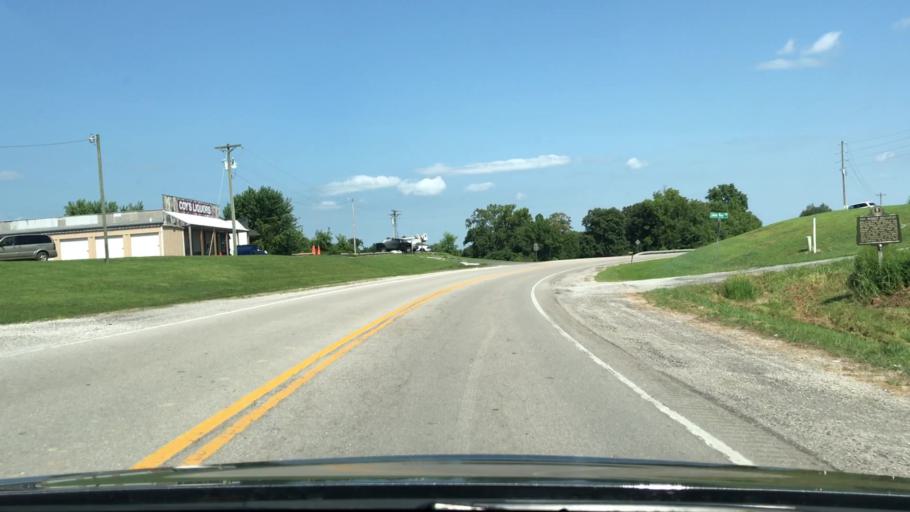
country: US
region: Kentucky
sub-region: Metcalfe County
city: Edmonton
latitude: 36.9893
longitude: -85.6555
